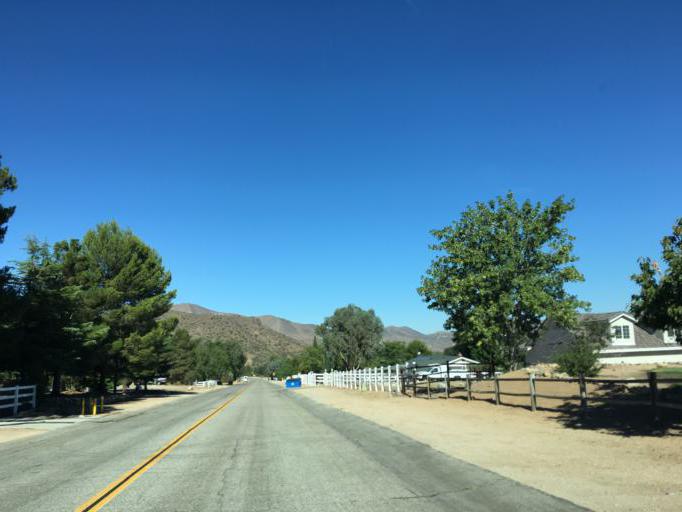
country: US
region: California
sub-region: Los Angeles County
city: Acton
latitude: 34.4646
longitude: -118.1723
